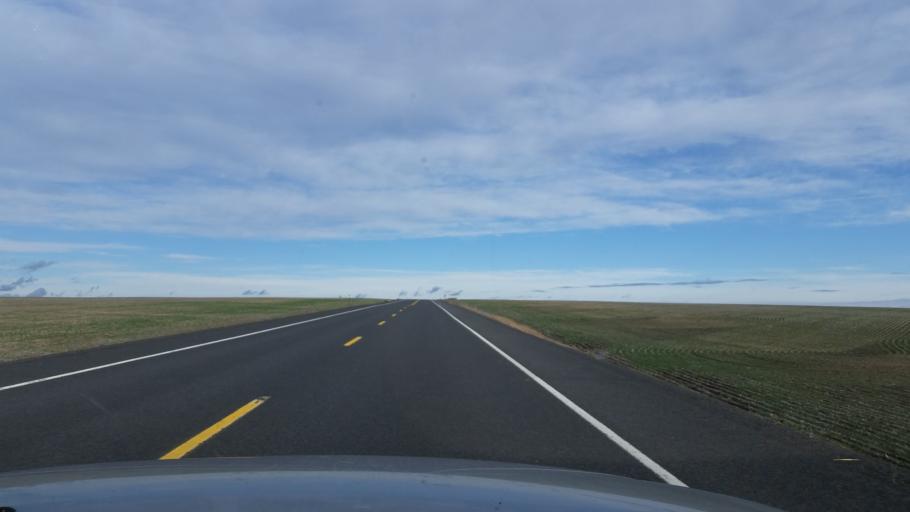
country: US
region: Washington
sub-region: Adams County
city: Ritzville
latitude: 47.3792
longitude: -118.4330
